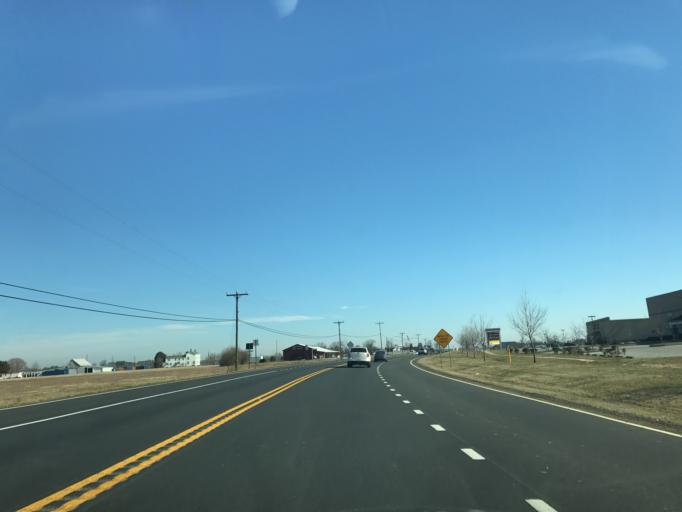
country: US
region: Delaware
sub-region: New Castle County
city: Middletown
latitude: 39.4352
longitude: -75.7572
